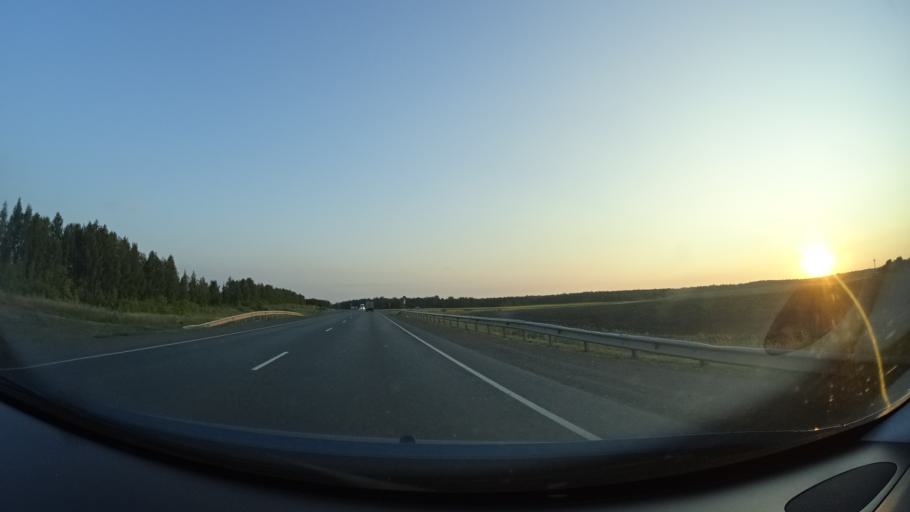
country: RU
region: Samara
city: Sernovodsk
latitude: 53.9280
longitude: 51.3227
